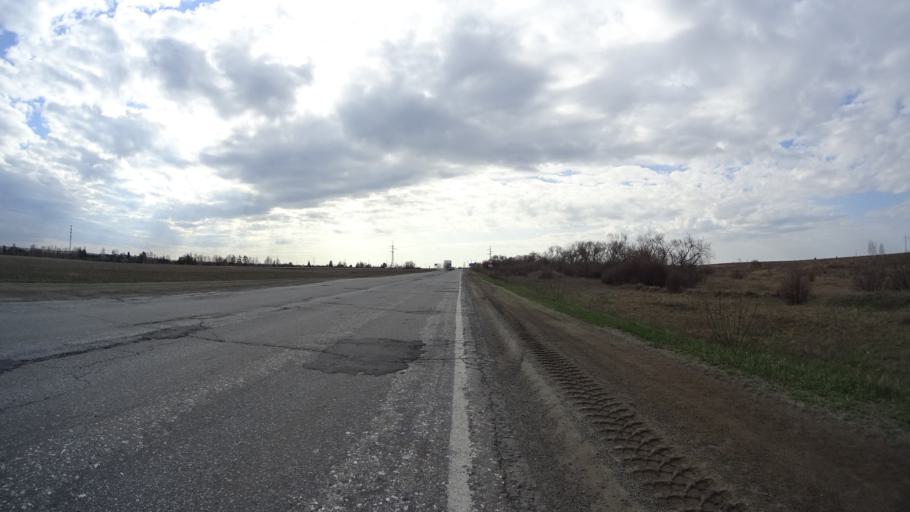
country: RU
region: Chelyabinsk
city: Troitsk
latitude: 54.0951
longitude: 61.4777
